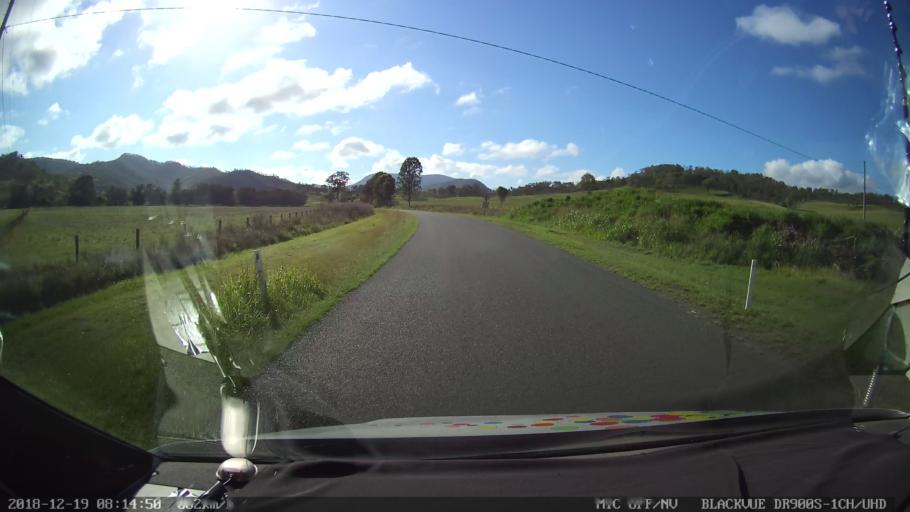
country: AU
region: New South Wales
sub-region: Kyogle
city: Kyogle
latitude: -28.2512
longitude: 152.8923
